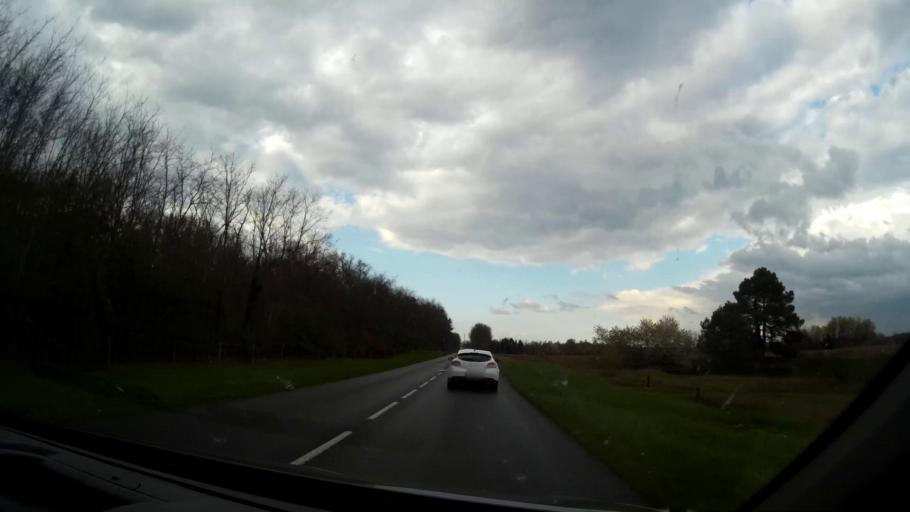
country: FR
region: Centre
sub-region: Departement du Loir-et-Cher
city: Cormeray
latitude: 47.4629
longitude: 1.4249
